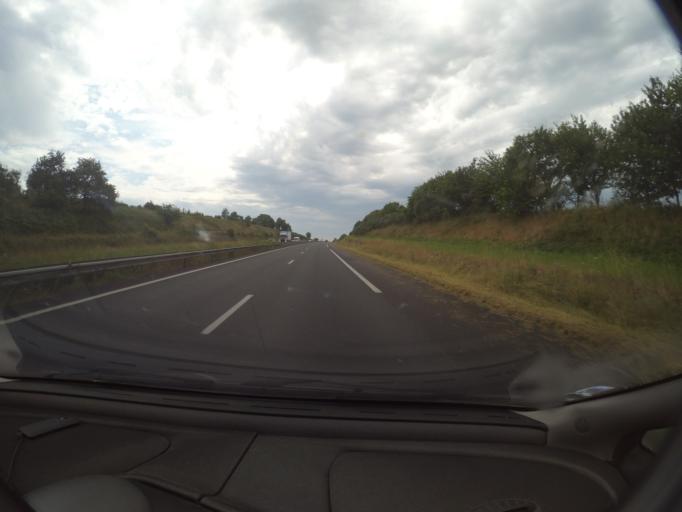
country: FR
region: Pays de la Loire
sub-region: Departement de la Loire-Atlantique
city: Couffe
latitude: 47.3777
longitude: -1.2648
